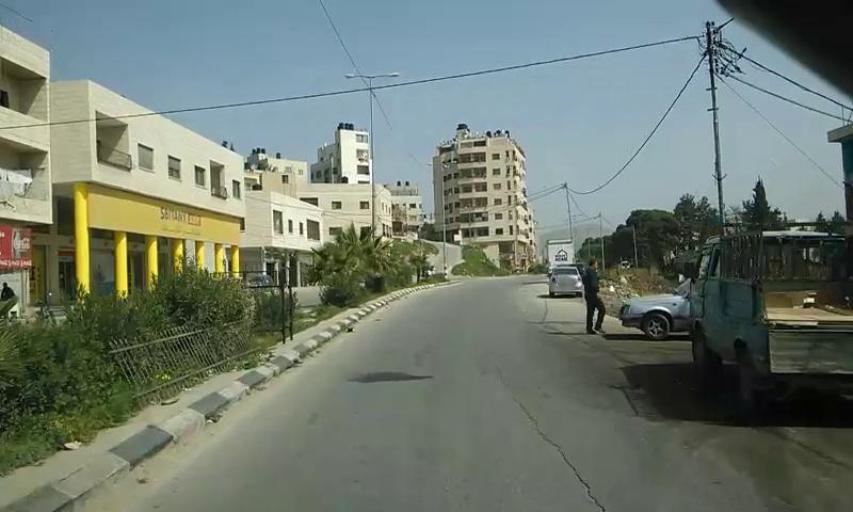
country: PS
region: West Bank
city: Balatah
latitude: 32.2166
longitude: 35.2912
